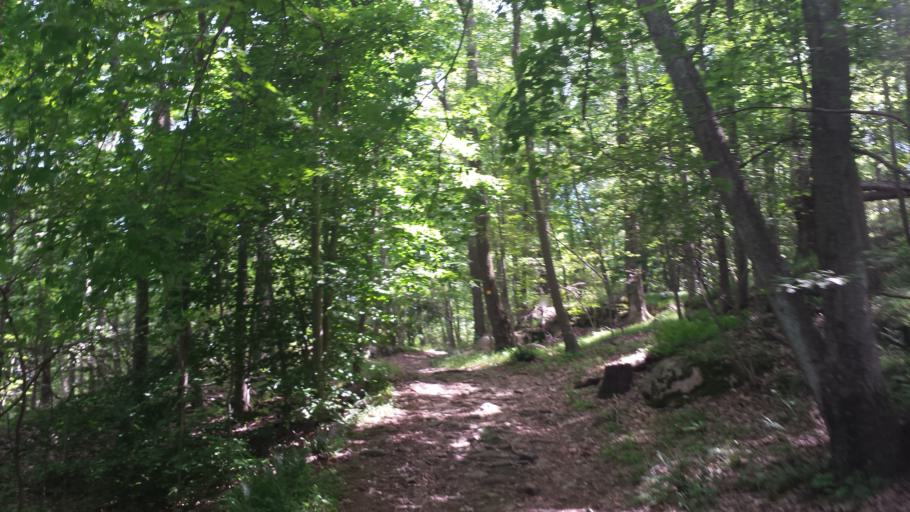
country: US
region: New York
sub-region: Westchester County
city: Pound Ridge
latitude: 41.2434
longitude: -73.5786
